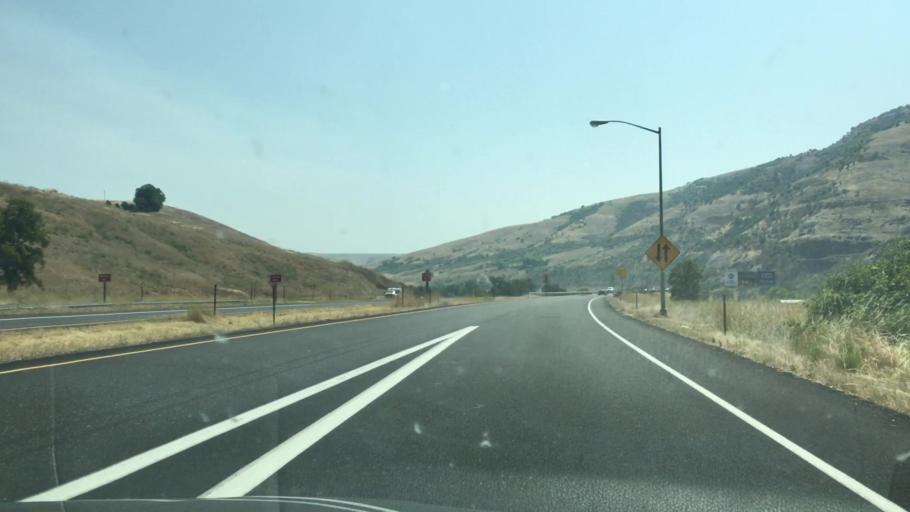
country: US
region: Idaho
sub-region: Nez Perce County
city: Lapwai
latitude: 46.4474
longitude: -116.8532
